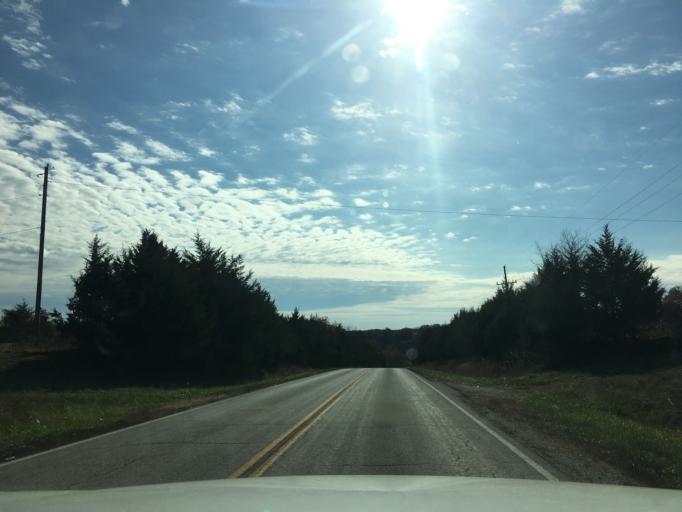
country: US
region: Missouri
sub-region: Osage County
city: Linn
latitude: 38.4010
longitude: -91.8200
